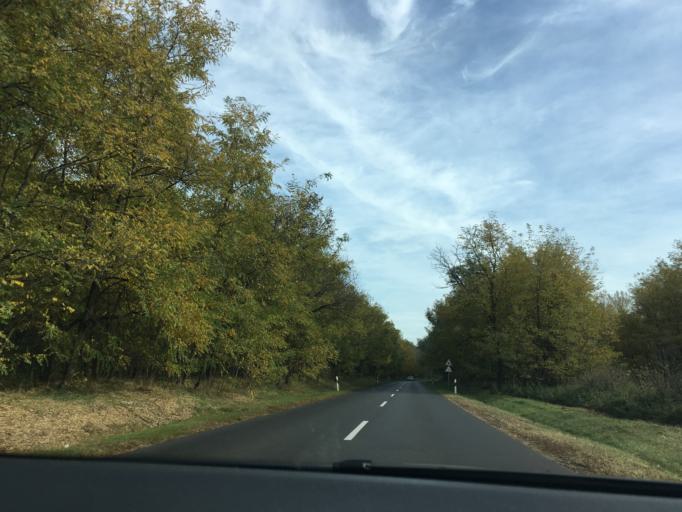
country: HU
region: Szabolcs-Szatmar-Bereg
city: Kisleta
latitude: 47.8518
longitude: 22.0284
